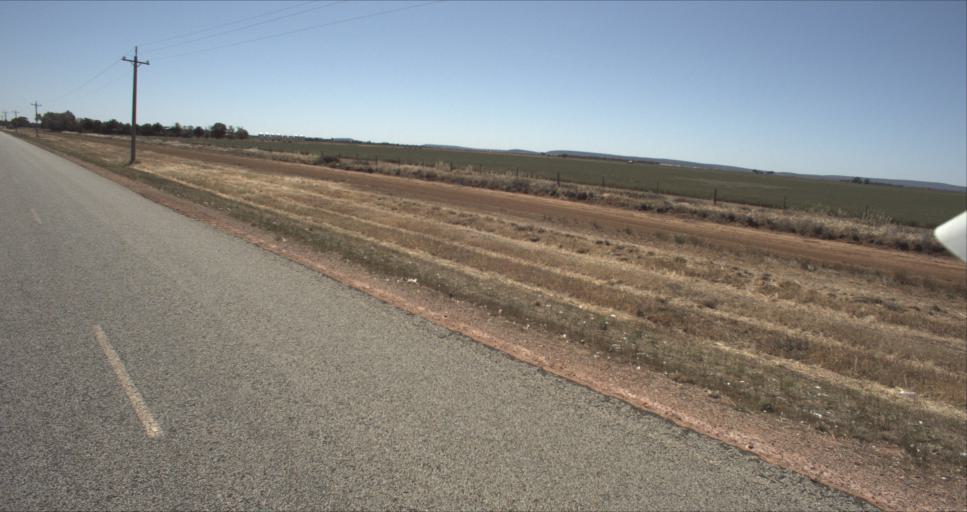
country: AU
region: New South Wales
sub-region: Leeton
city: Leeton
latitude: -34.4554
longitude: 146.2952
